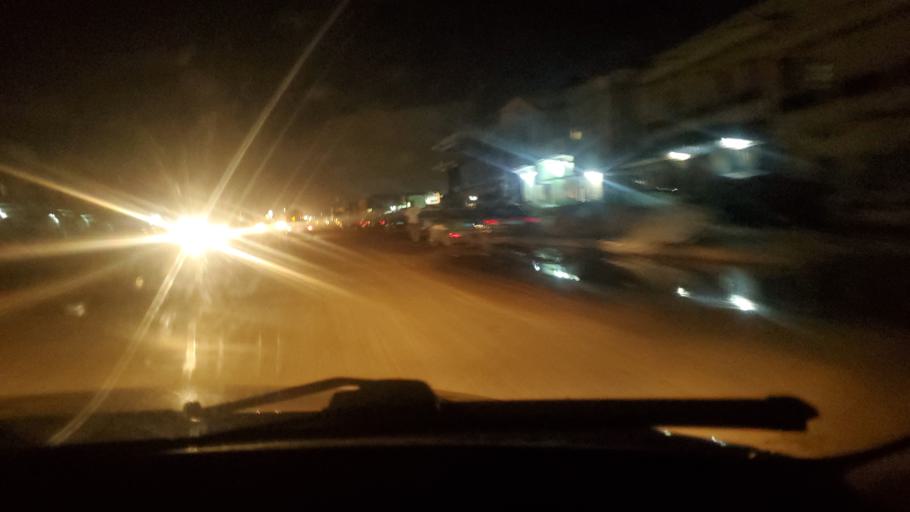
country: SN
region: Dakar
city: Pikine
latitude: 14.7448
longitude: -17.3825
